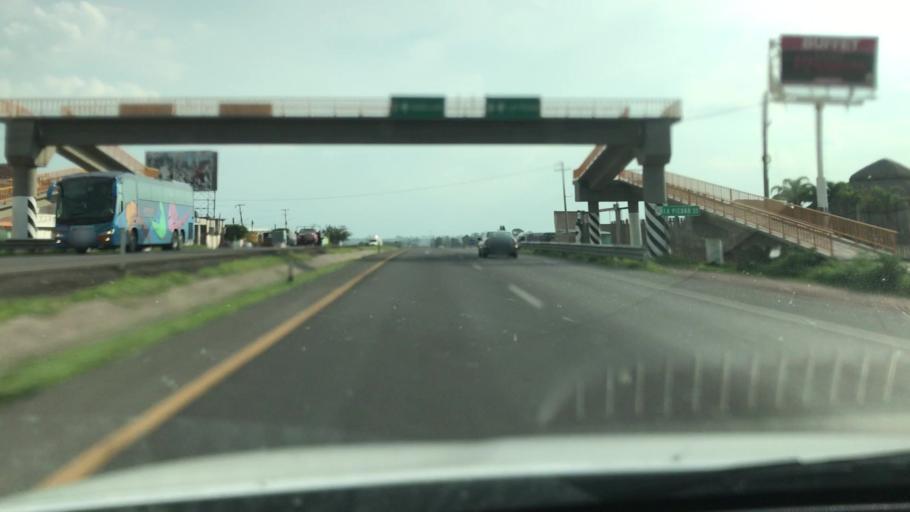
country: MX
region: Guanajuato
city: Penjamo
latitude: 20.4165
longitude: -101.7283
